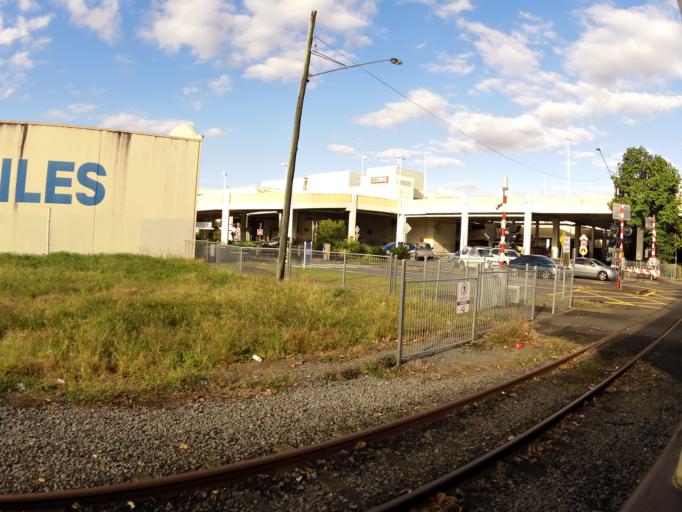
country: AU
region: Queensland
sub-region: Cairns
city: Cairns
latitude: -16.9237
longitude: 145.7697
